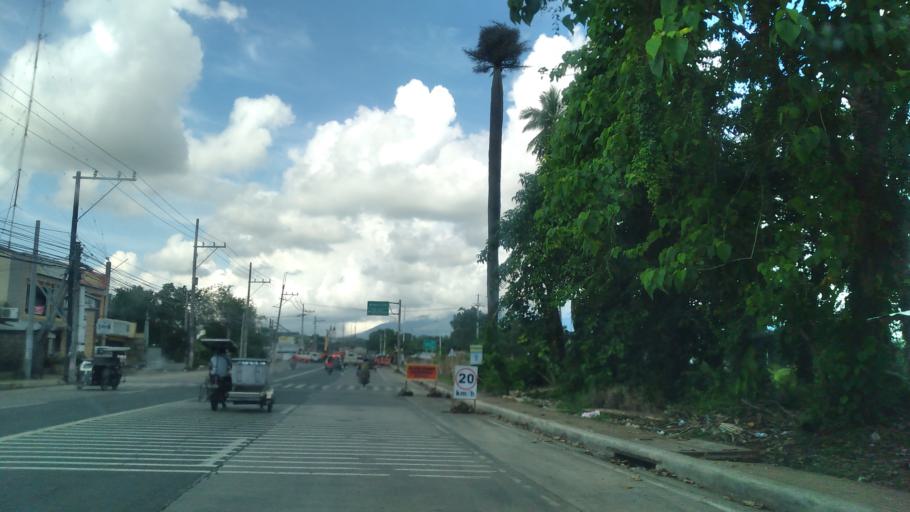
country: PH
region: Calabarzon
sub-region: Province of Quezon
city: Isabang
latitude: 13.9509
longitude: 121.5789
